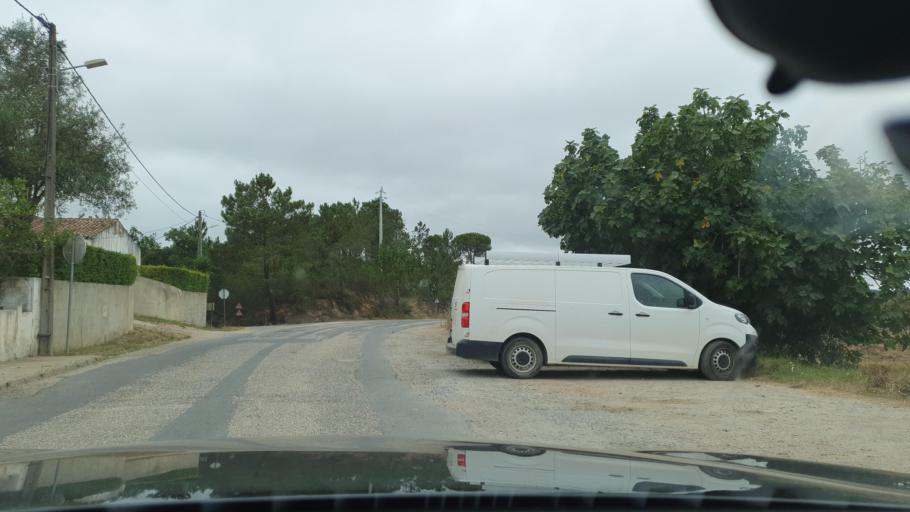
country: PT
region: Beja
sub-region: Odemira
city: Sao Teotonio
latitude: 37.5065
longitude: -8.6951
